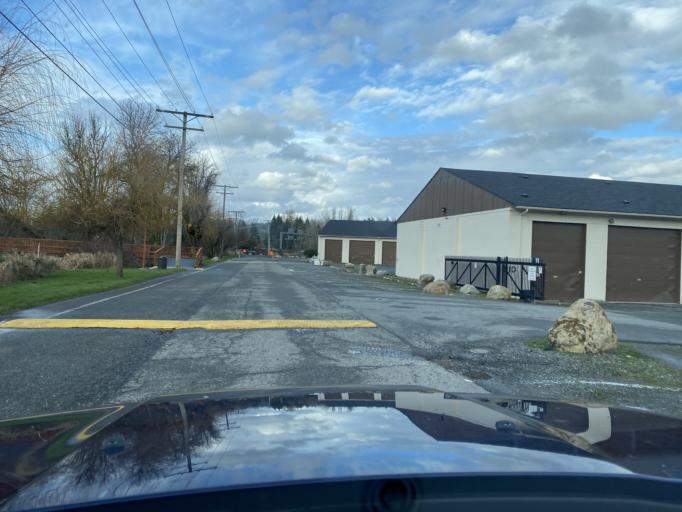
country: US
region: Washington
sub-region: King County
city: Issaquah
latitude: 47.5488
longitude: -122.0680
